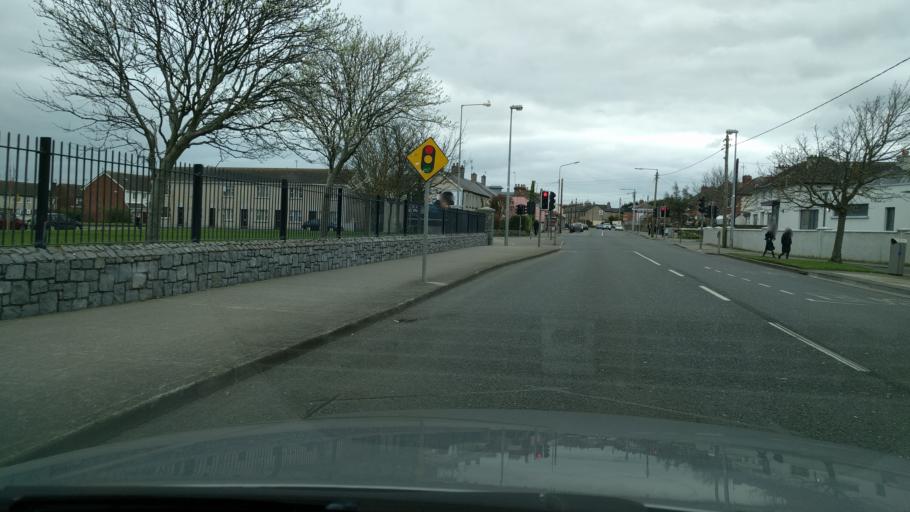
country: IE
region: Leinster
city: Balbriggan
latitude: 53.6138
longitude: -6.1896
